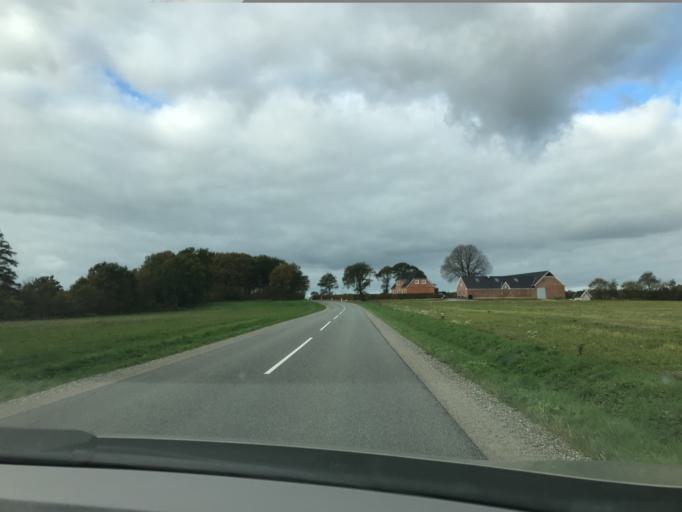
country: DK
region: South Denmark
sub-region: Varde Kommune
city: Olgod
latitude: 55.7934
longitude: 8.7535
